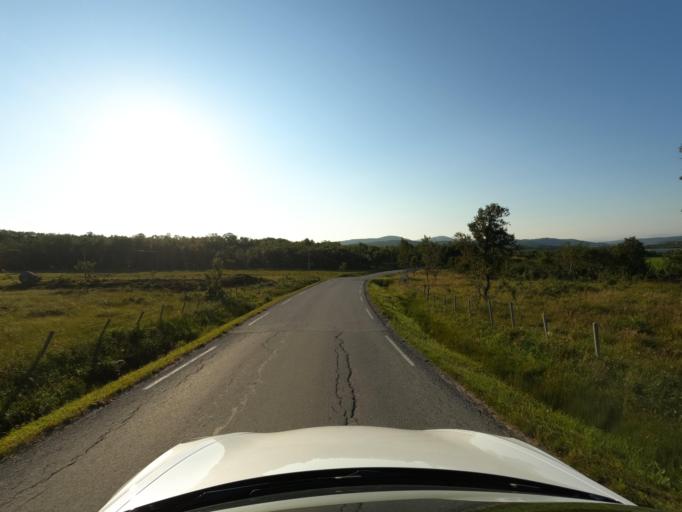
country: NO
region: Troms
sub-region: Skanland
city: Evenskjer
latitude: 68.4593
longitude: 16.6819
